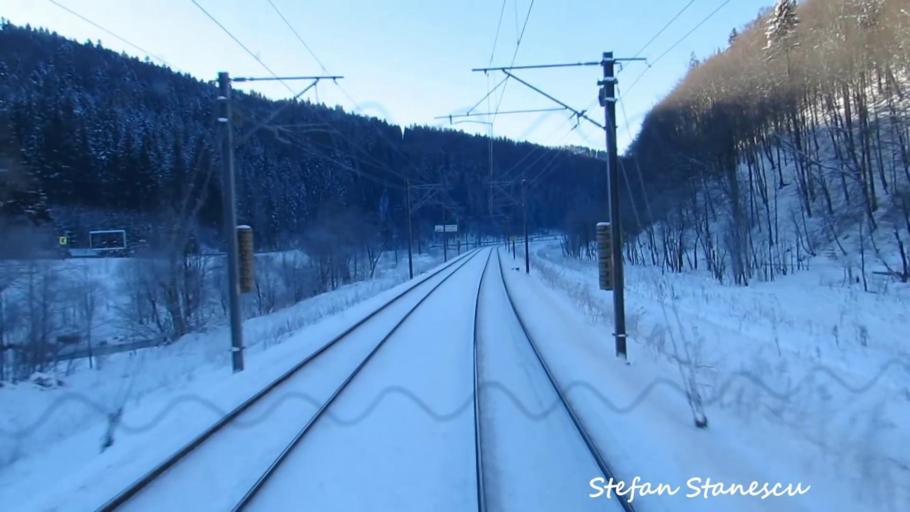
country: RO
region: Prahova
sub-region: Oras Azuga
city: Azuga
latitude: 45.4599
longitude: 25.5658
